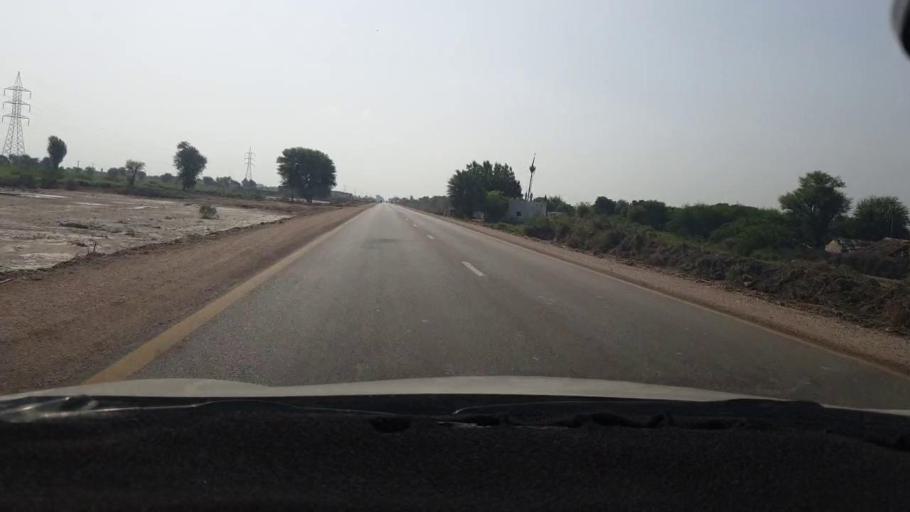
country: PK
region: Sindh
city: Jhol
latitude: 25.9160
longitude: 69.0086
